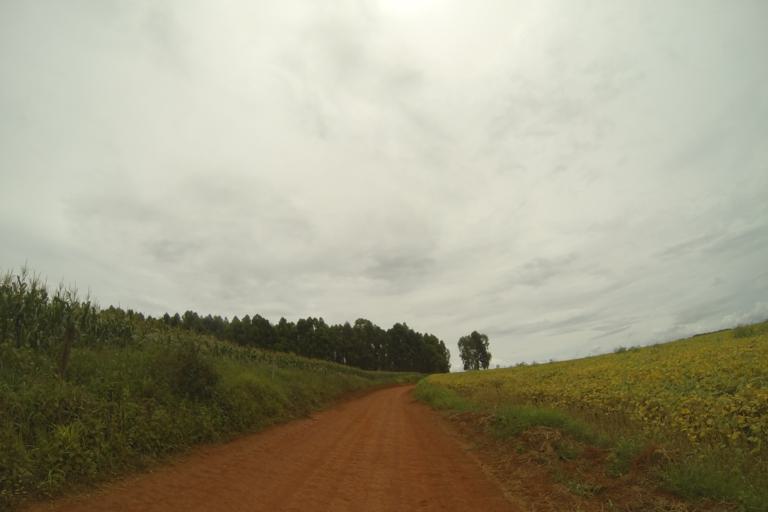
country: BR
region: Minas Gerais
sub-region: Ibia
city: Ibia
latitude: -19.7435
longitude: -46.6330
